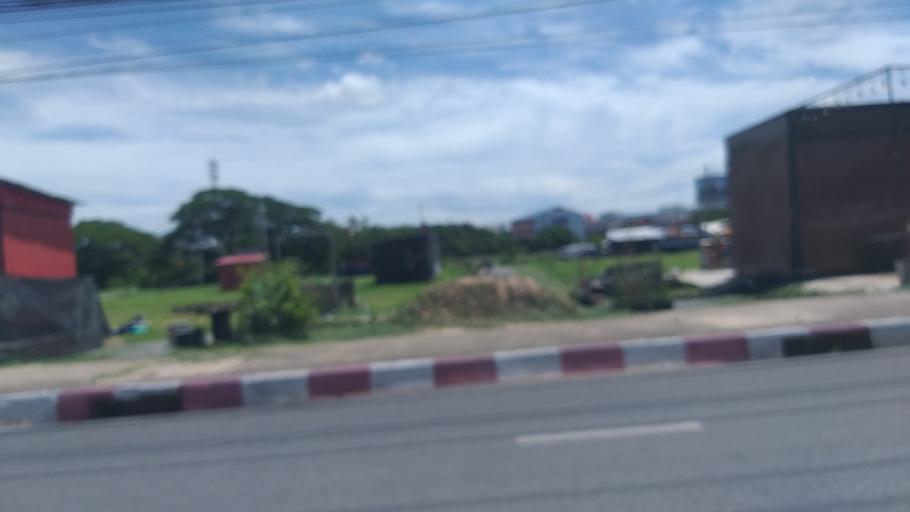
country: TH
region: Khon Kaen
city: Khon Kaen
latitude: 16.4323
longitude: 102.8226
